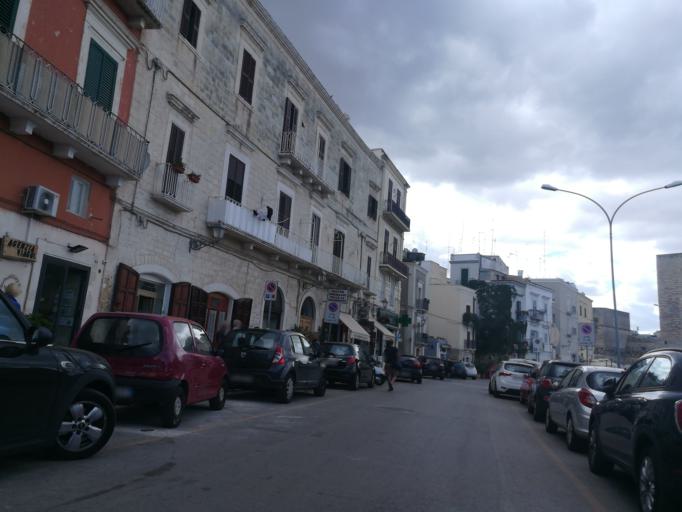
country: IT
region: Apulia
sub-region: Provincia di Bari
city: Bari
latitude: 41.1298
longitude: 16.8681
